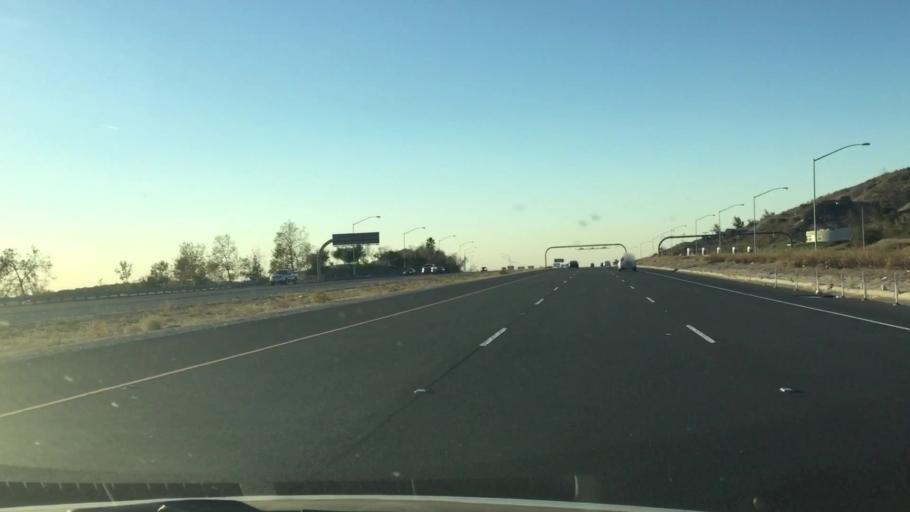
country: US
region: California
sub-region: Orange County
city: Foothill Ranch
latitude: 33.6995
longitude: -117.7003
